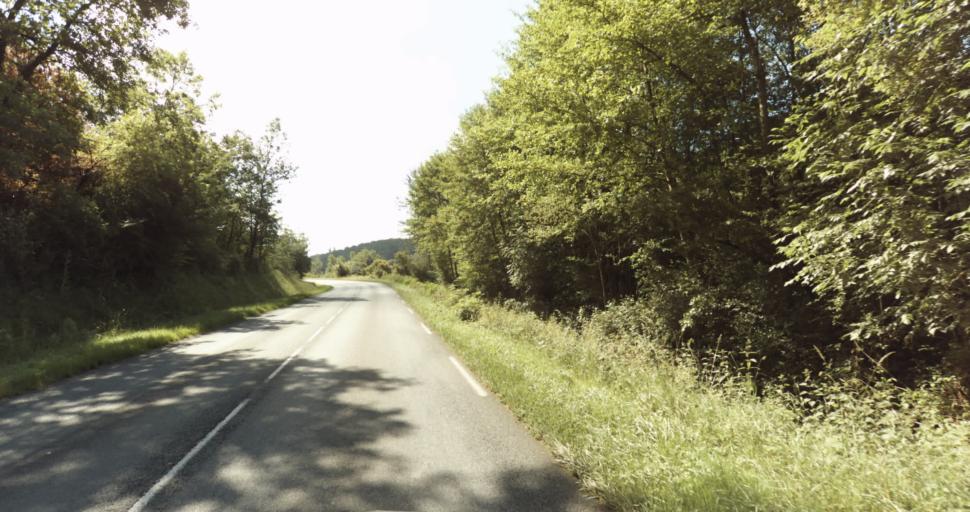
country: FR
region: Aquitaine
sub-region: Departement de la Dordogne
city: Lalinde
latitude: 44.8499
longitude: 0.8119
